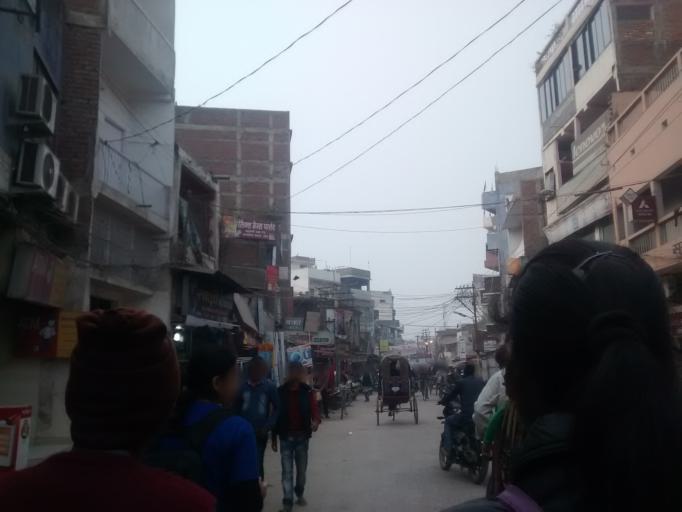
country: IN
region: Bihar
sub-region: Muzaffarpur
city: Muzaffarpur
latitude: 26.1182
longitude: 85.3920
